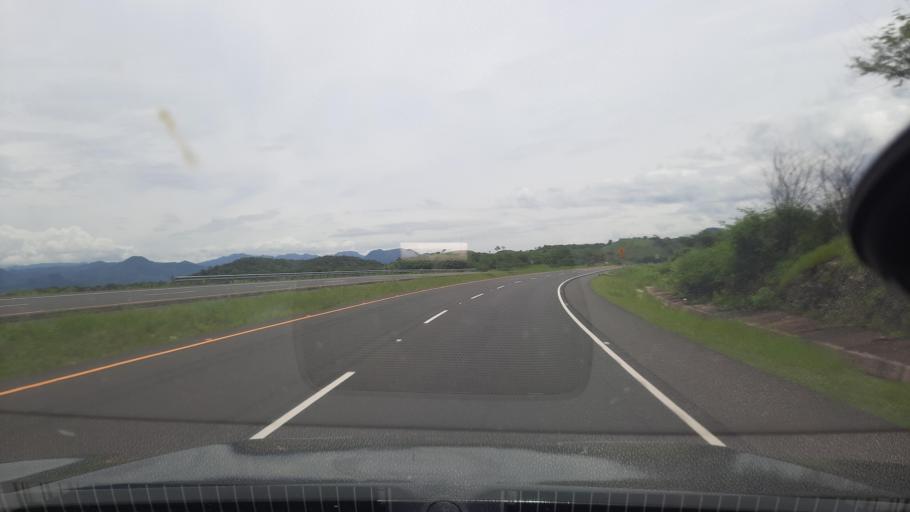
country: HN
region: Valle
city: Aramecina
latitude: 13.7373
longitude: -87.7202
